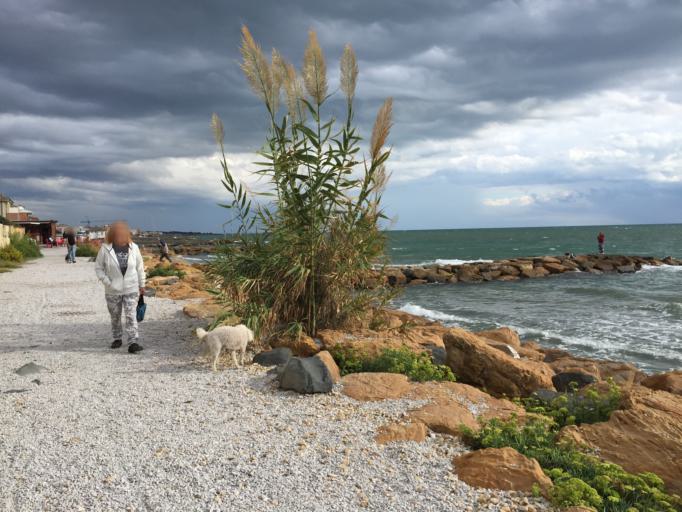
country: IT
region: Latium
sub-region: Citta metropolitana di Roma Capitale
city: Ladispoli
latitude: 41.9528
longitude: 12.0628
